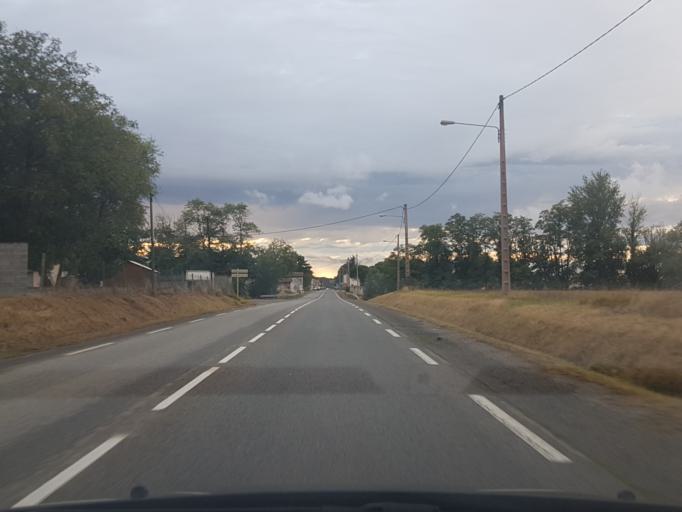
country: FR
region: Midi-Pyrenees
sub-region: Departement de l'Ariege
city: Mirepoix
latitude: 43.0777
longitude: 1.7691
